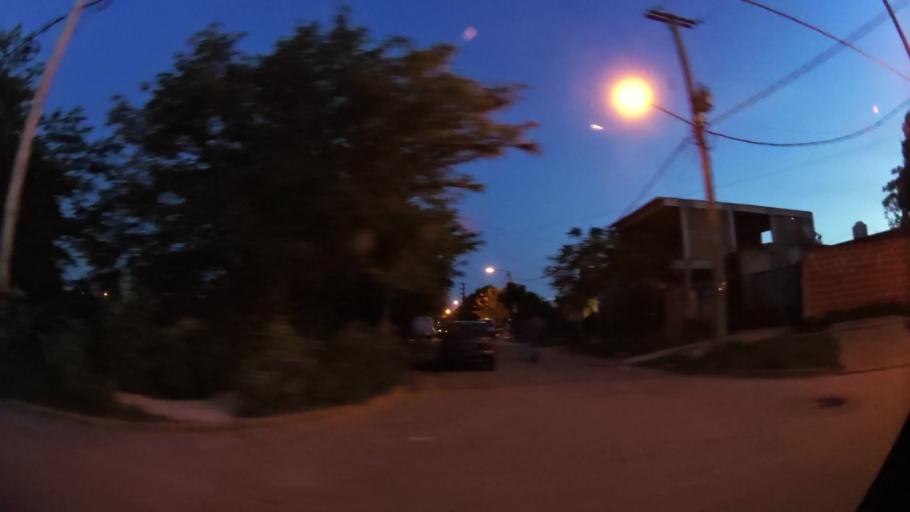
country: AR
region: Buenos Aires
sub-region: Partido de Quilmes
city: Quilmes
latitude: -34.7597
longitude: -58.1953
